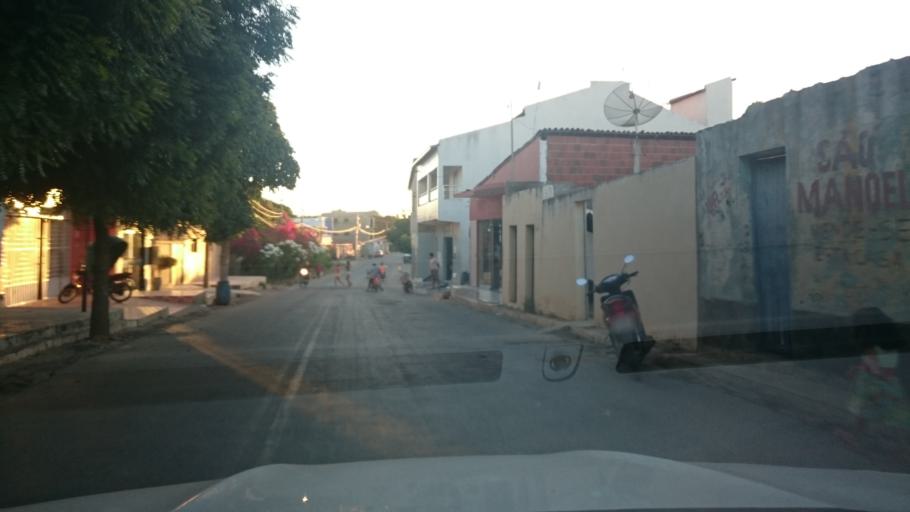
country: BR
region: Rio Grande do Norte
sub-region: Umarizal
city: Umarizal
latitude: -6.0250
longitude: -37.9890
